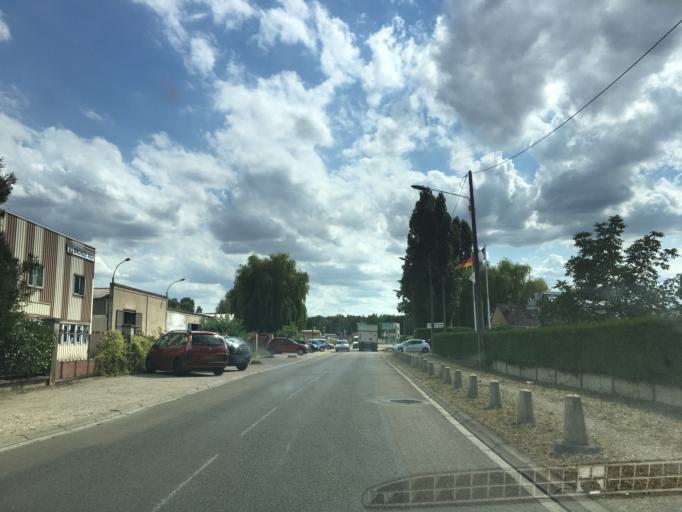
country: FR
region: Bourgogne
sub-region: Departement de l'Yonne
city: Joigny
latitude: 47.9758
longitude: 3.3860
